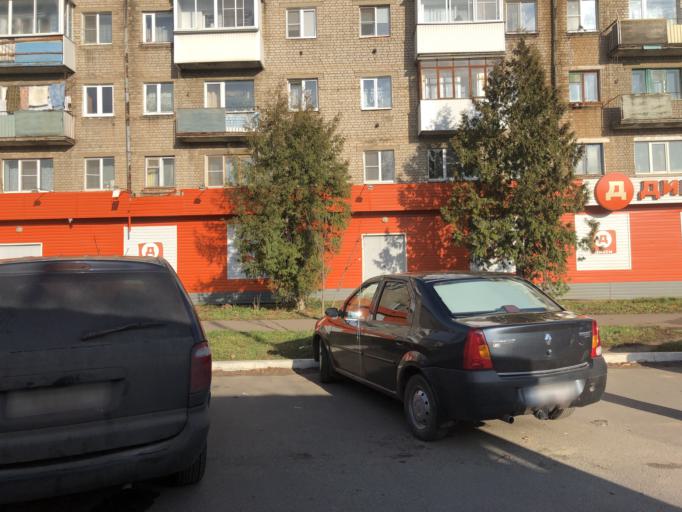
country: RU
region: Tverskaya
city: Rzhev
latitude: 56.2644
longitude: 34.3280
